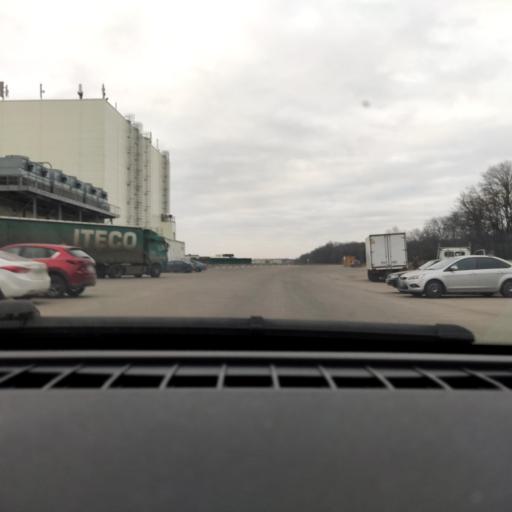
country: RU
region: Voronezj
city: Podgornoye
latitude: 51.7873
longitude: 39.2059
